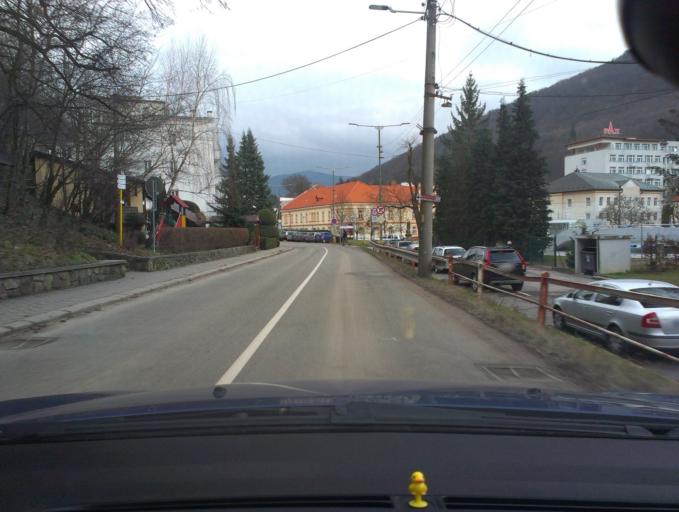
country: SK
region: Nitriansky
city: Trencianske Teplice
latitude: 48.9102
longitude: 18.1711
